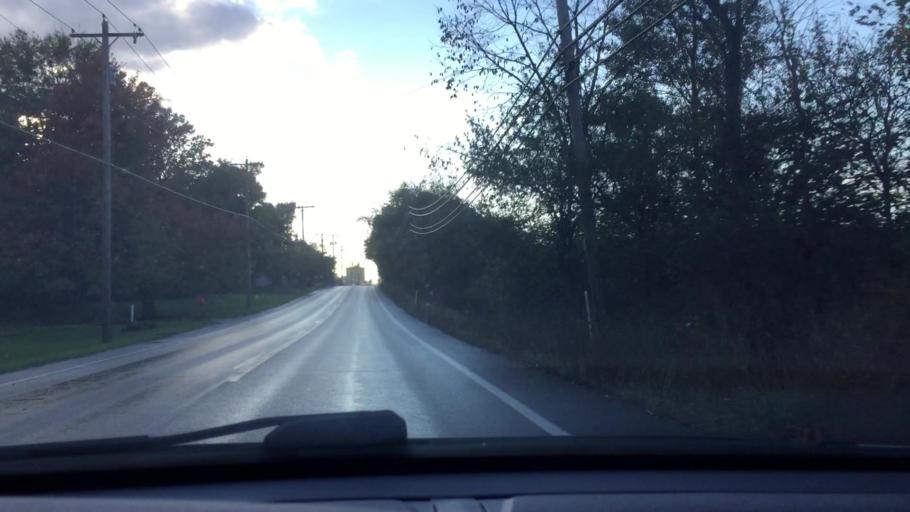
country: US
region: Pennsylvania
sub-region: Lawrence County
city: Bessemer
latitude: 40.9760
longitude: -80.4661
